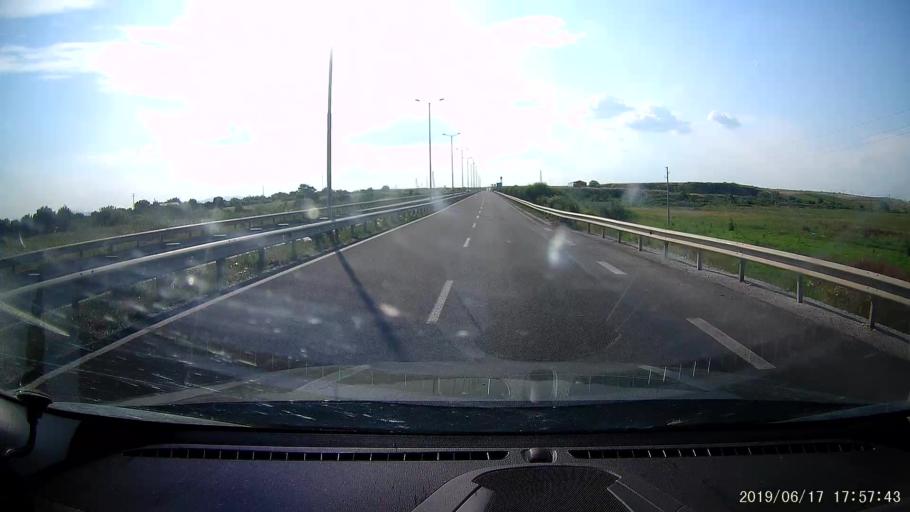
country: GR
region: East Macedonia and Thrace
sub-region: Nomos Evrou
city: Rizia
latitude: 41.7226
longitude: 26.3313
